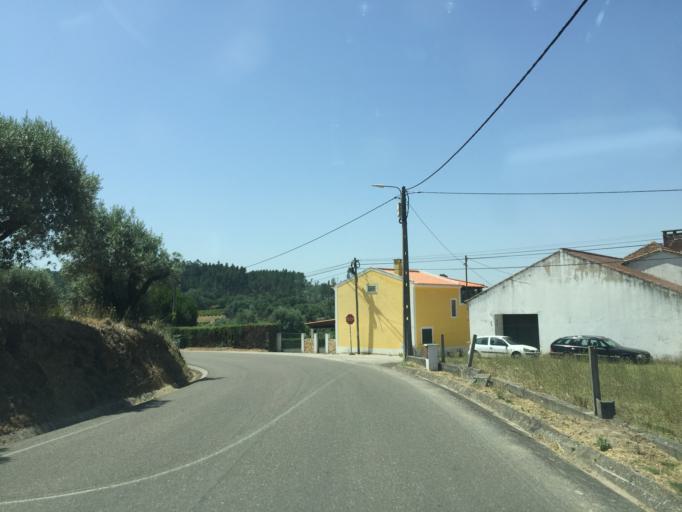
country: PT
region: Santarem
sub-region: Ferreira do Zezere
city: Ferreira do Zezere
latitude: 39.6181
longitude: -8.3120
